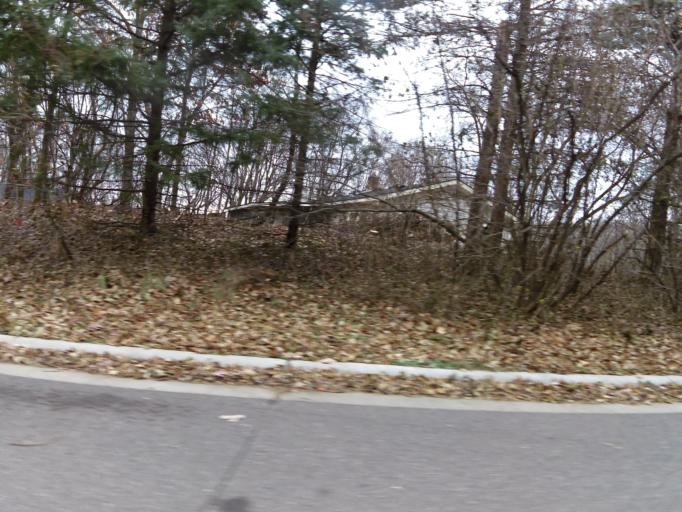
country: US
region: Minnesota
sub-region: Washington County
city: Lake Elmo
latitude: 44.9786
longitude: -92.8808
